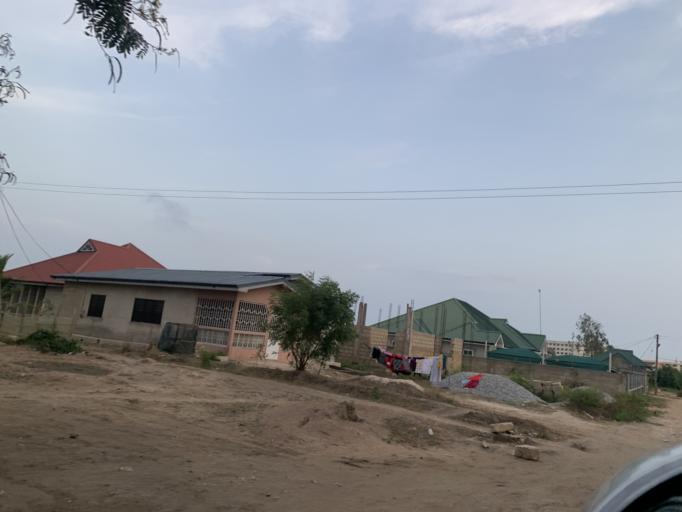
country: GH
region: Central
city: Winneba
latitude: 5.3756
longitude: -0.6320
